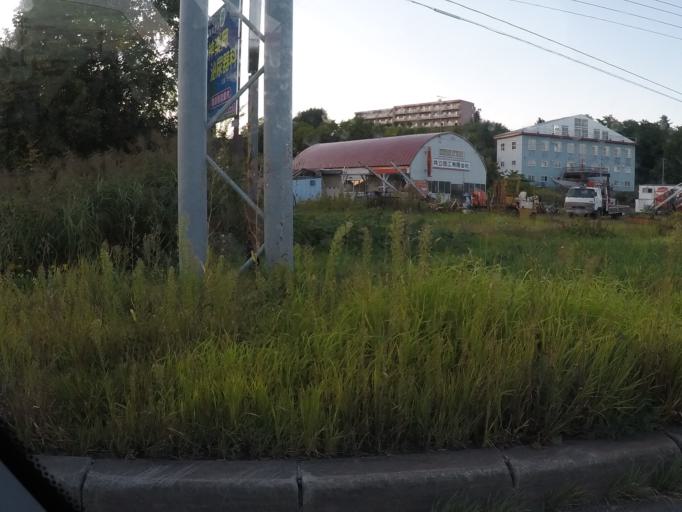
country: JP
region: Hokkaido
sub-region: Asahikawa-shi
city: Asahikawa
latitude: 43.5976
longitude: 142.4637
